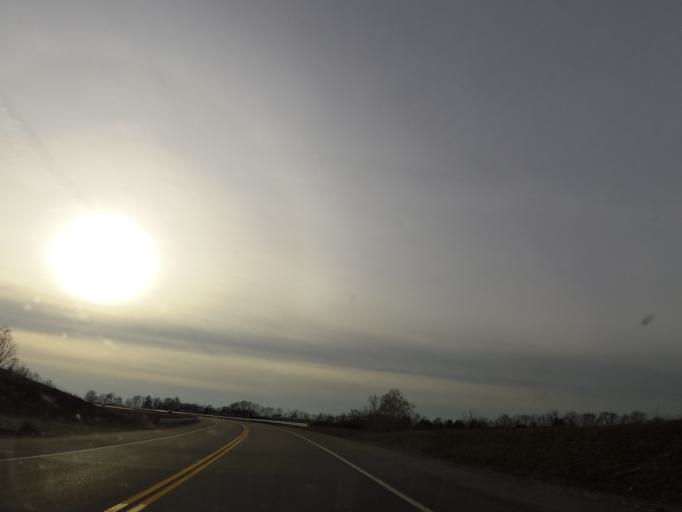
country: US
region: Kentucky
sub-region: Harrison County
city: Cynthiana
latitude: 38.3977
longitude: -84.3161
